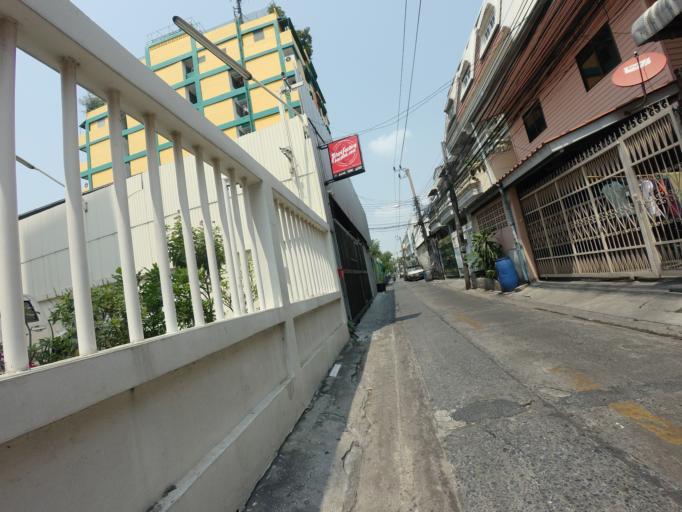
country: TH
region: Bangkok
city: Din Daeng
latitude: 13.7652
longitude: 100.5644
